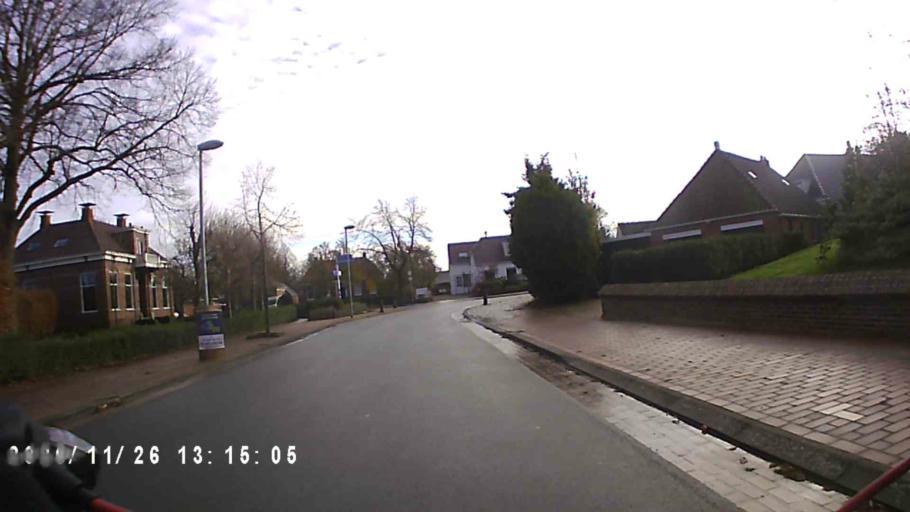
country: NL
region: Groningen
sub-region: Gemeente Appingedam
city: Appingedam
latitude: 53.3580
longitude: 6.8709
